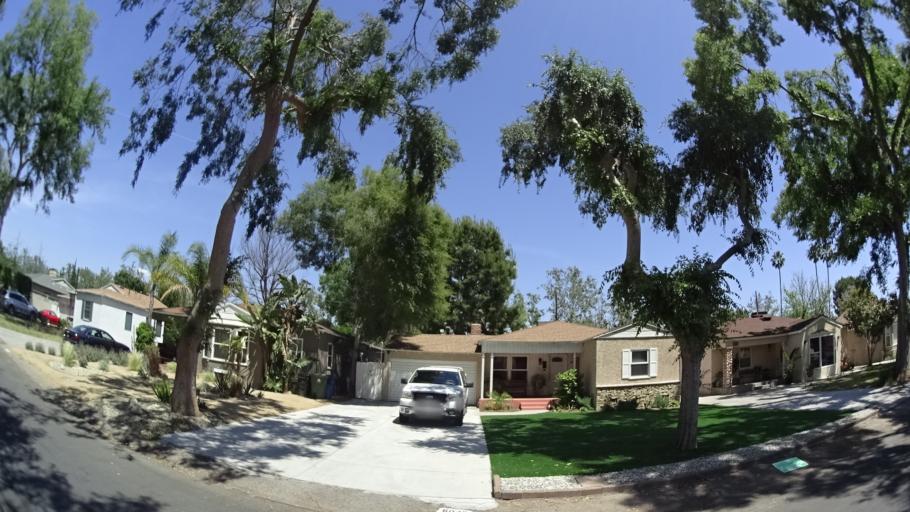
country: US
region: California
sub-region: Los Angeles County
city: North Hollywood
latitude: 34.1807
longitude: -118.3900
